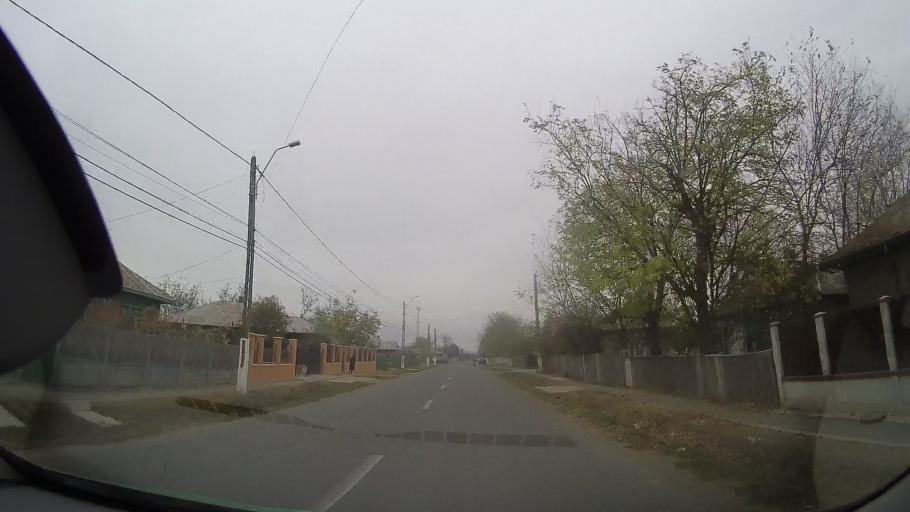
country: RO
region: Braila
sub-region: Comuna Budesti
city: Tataru
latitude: 44.8463
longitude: 27.4279
